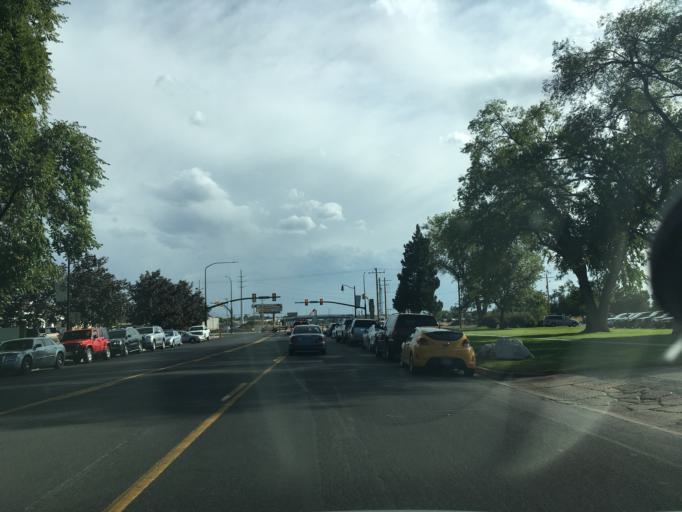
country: US
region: Utah
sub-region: Davis County
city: Layton
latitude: 41.0612
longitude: -111.9611
